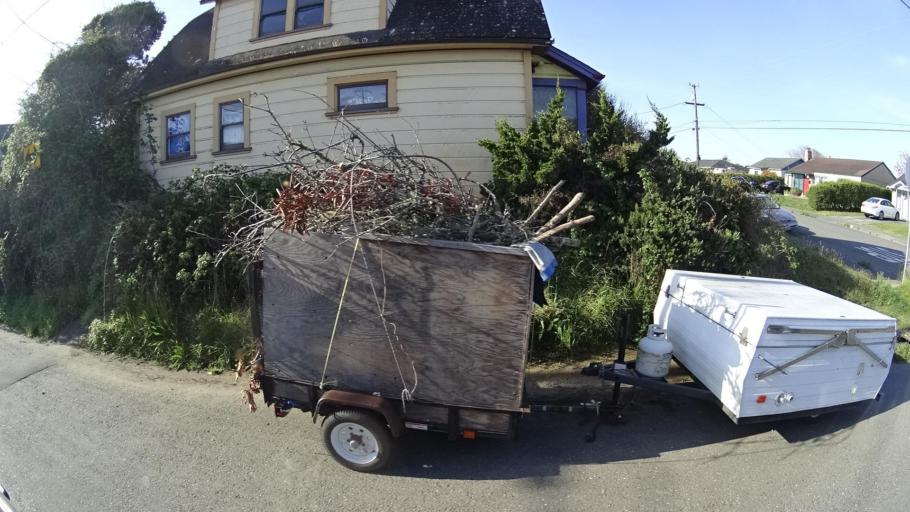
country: US
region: California
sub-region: Humboldt County
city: Bayview
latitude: 40.7758
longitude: -124.1761
